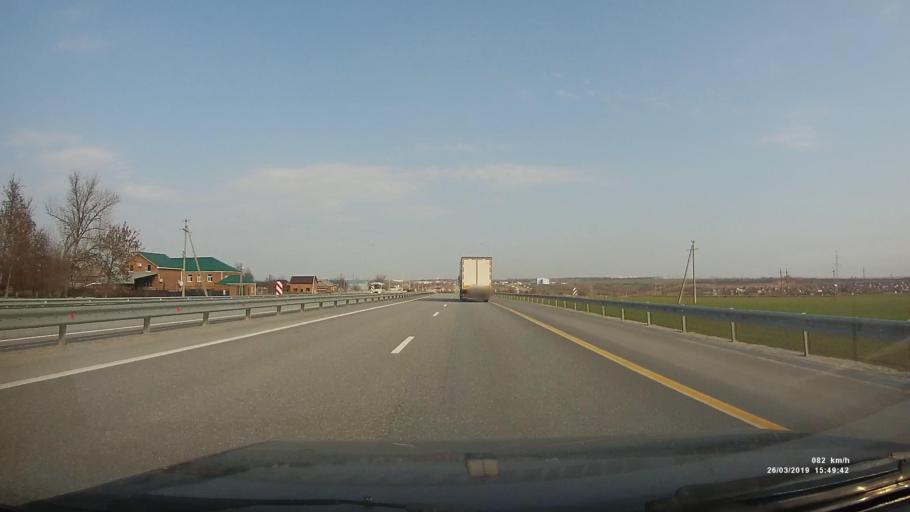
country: RU
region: Rostov
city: Chaltyr
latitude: 47.2752
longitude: 39.4735
